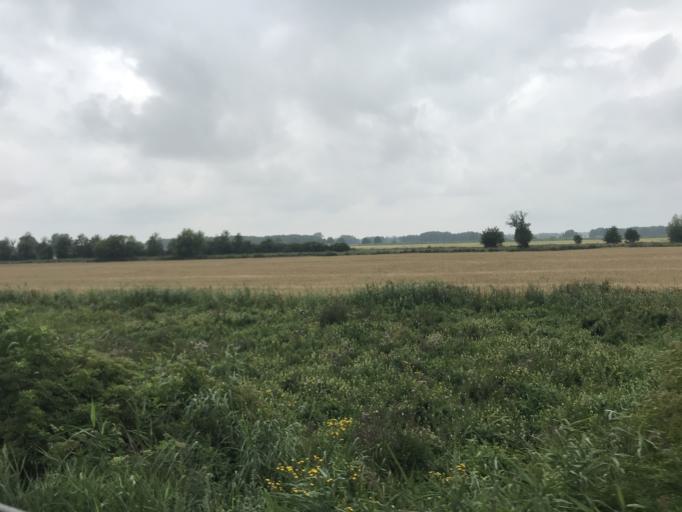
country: PL
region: Warmian-Masurian Voivodeship
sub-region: Powiat elblaski
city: Gronowo Elblaskie
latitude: 54.1037
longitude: 19.3324
